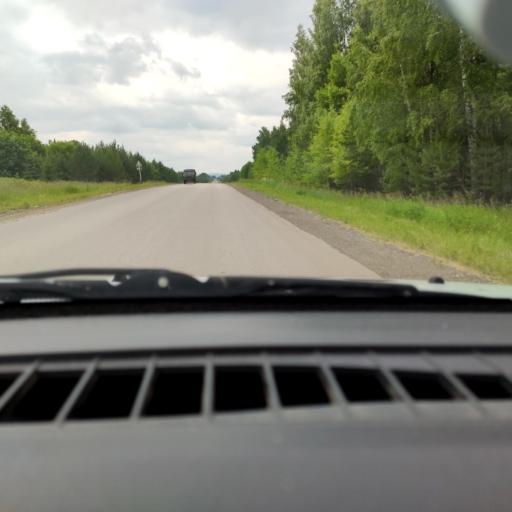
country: RU
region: Perm
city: Orda
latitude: 57.1209
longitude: 56.6749
